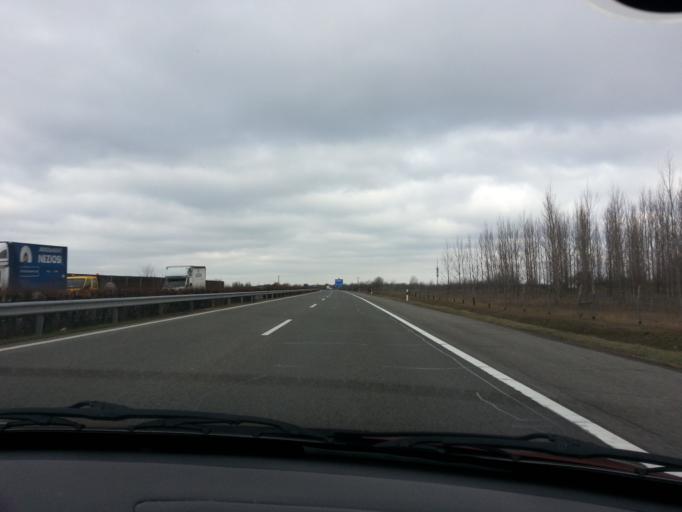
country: HU
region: Bacs-Kiskun
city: Kiskunfelegyhaza
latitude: 46.6625
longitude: 19.8315
